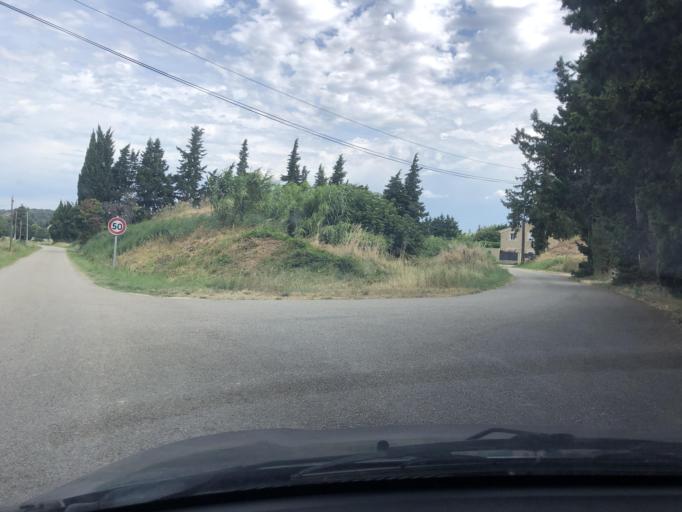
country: FR
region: Provence-Alpes-Cote d'Azur
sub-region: Departement du Vaucluse
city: Piolenc
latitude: 44.1565
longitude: 4.7619
